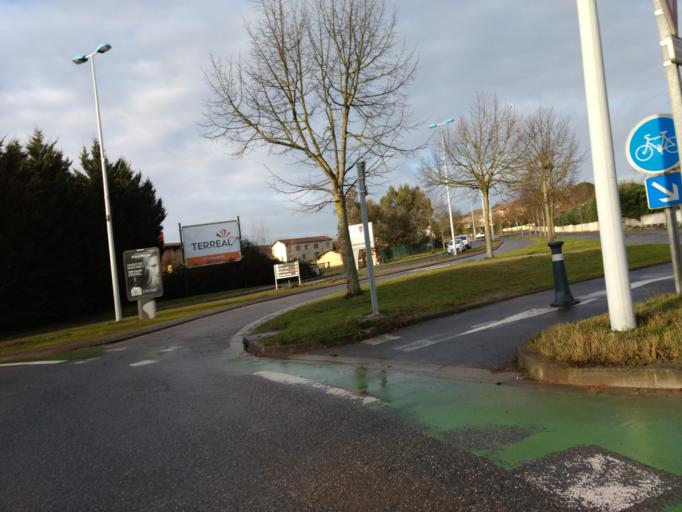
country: FR
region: Midi-Pyrenees
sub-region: Departement de la Haute-Garonne
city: Colomiers
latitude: 43.6124
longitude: 1.3181
